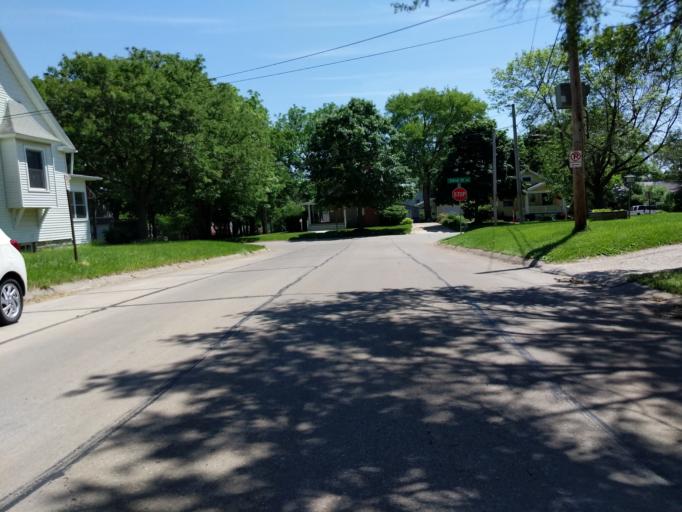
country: US
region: Iowa
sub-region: Linn County
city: Cedar Rapids
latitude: 42.0104
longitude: -91.6410
